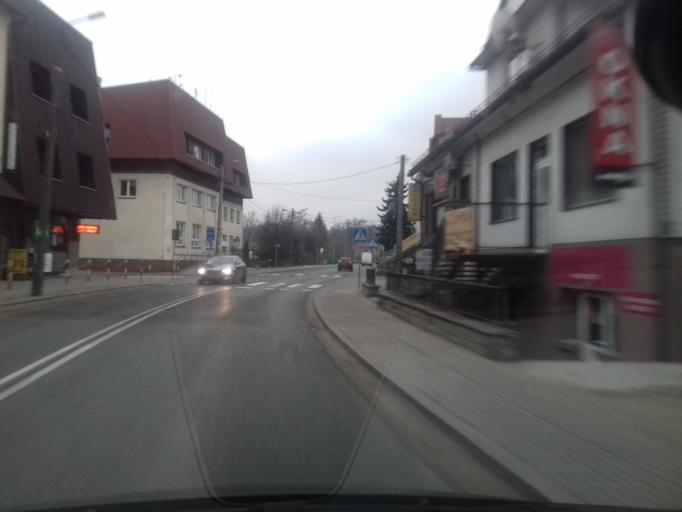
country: PL
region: Lesser Poland Voivodeship
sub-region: Powiat limanowski
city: Mszana Dolna
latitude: 49.6753
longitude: 20.0819
